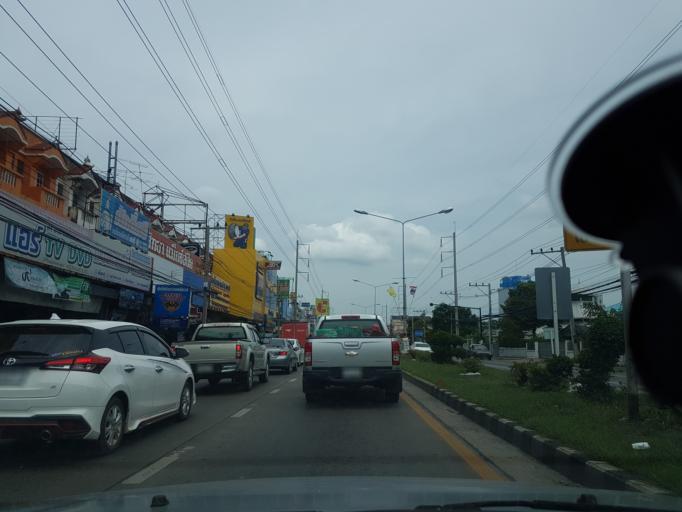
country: TH
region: Lop Buri
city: Lop Buri
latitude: 14.7942
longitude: 100.6684
